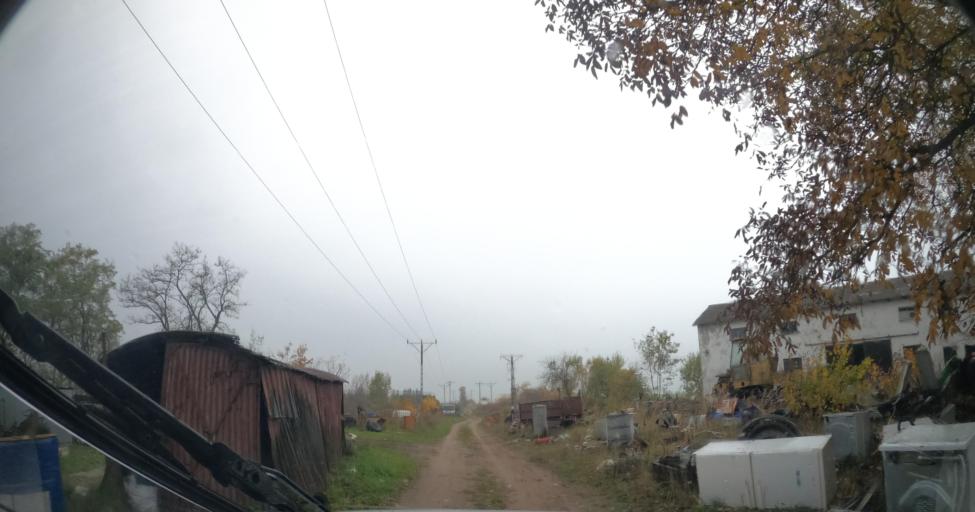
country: PL
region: West Pomeranian Voivodeship
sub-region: Powiat drawski
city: Drawsko Pomorskie
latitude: 53.5238
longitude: 15.7876
